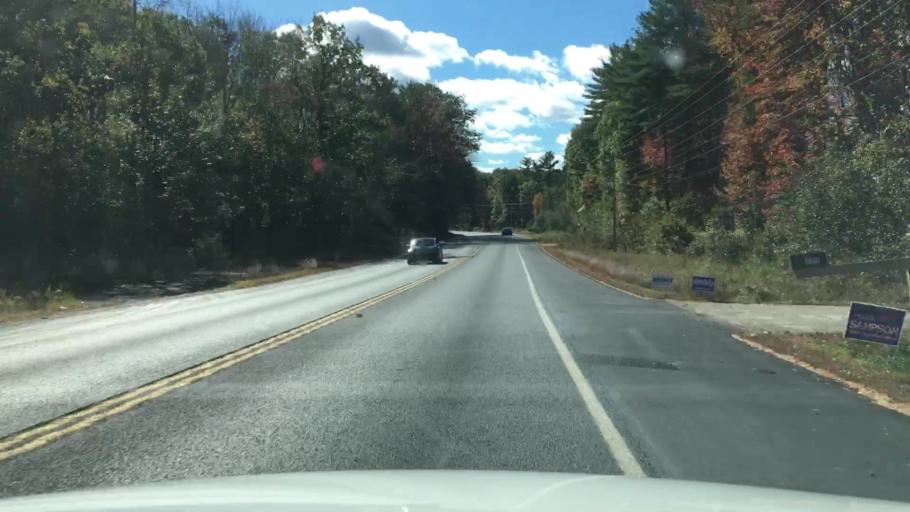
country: US
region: Maine
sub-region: York County
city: Alfred
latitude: 43.4474
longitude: -70.7280
